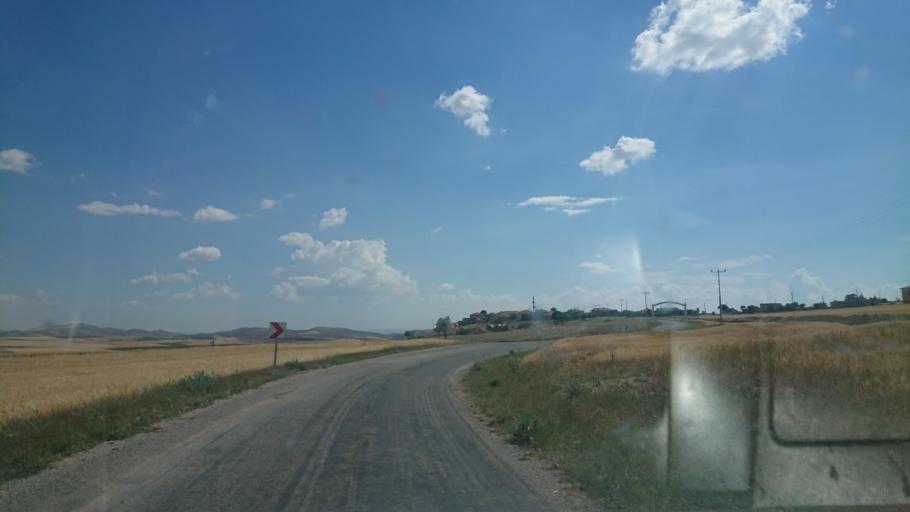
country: TR
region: Aksaray
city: Agacoren
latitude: 38.7561
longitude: 33.7808
